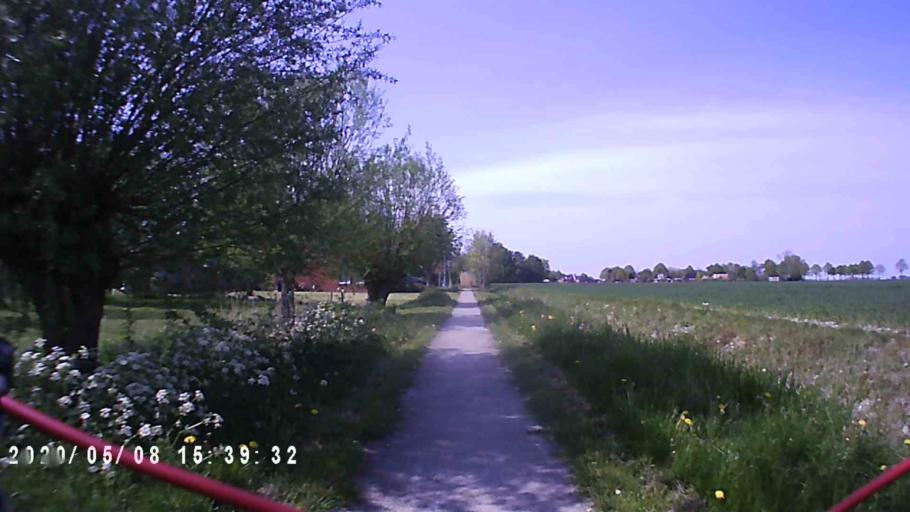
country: NL
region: Groningen
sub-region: Gemeente Bedum
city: Bedum
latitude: 53.3674
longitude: 6.7180
